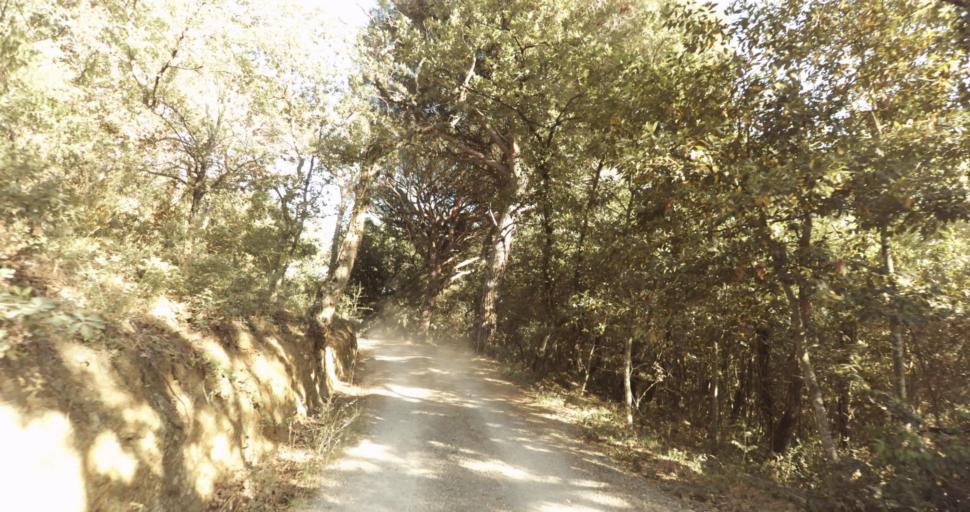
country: FR
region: Provence-Alpes-Cote d'Azur
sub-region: Departement du Var
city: Gassin
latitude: 43.2238
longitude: 6.5810
